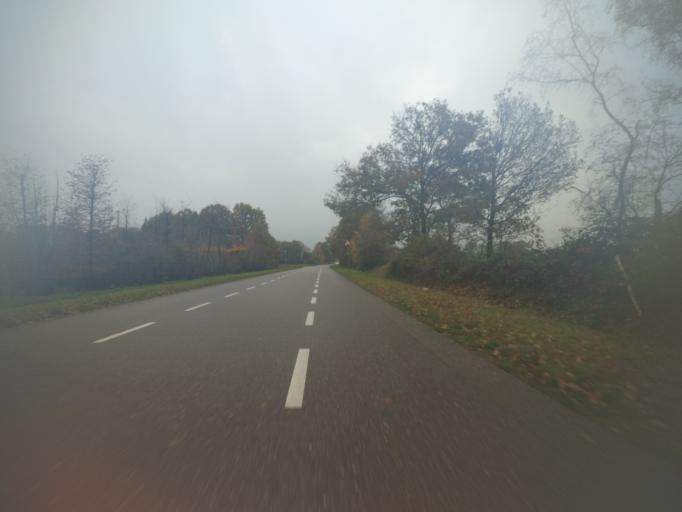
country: NL
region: Gelderland
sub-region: Gemeente Ede
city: Lunteren
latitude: 52.0977
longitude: 5.5925
